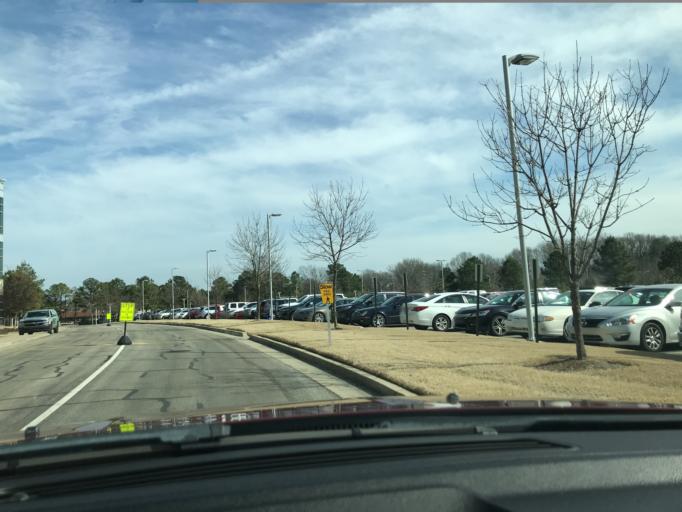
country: US
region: Tennessee
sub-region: Shelby County
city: Germantown
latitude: 35.0497
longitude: -89.7862
